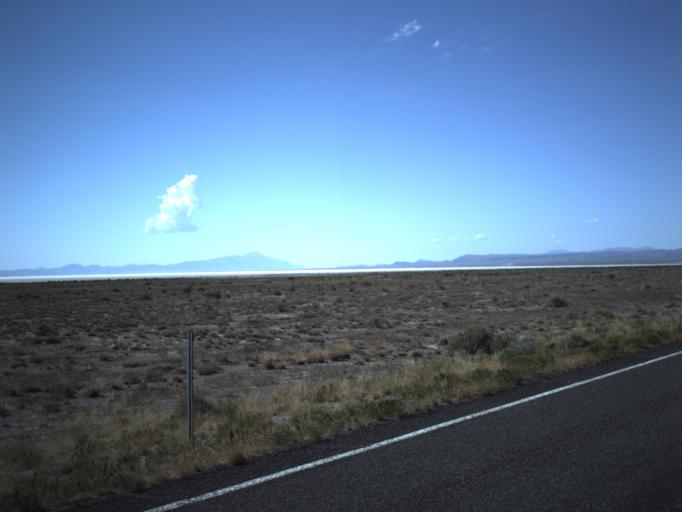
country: US
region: Utah
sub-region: Millard County
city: Delta
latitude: 39.1036
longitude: -113.1490
